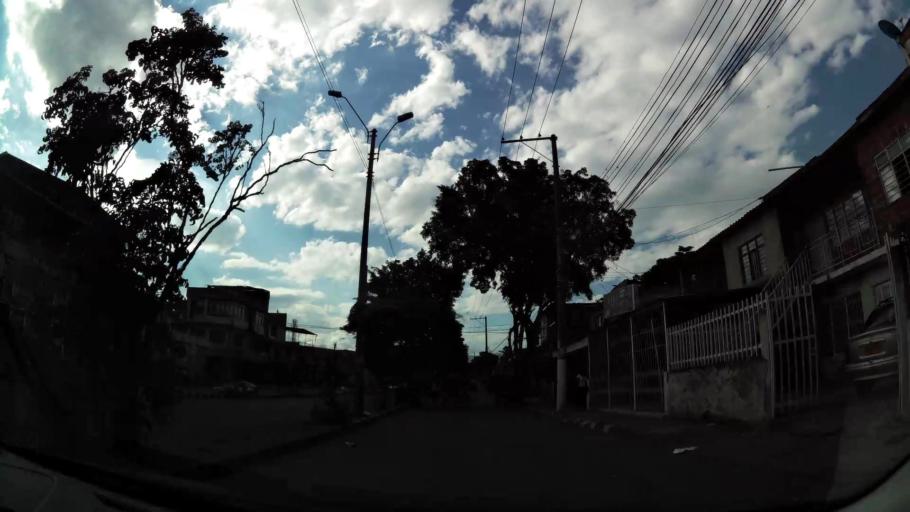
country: CO
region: Valle del Cauca
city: Cali
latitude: 3.4145
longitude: -76.4929
